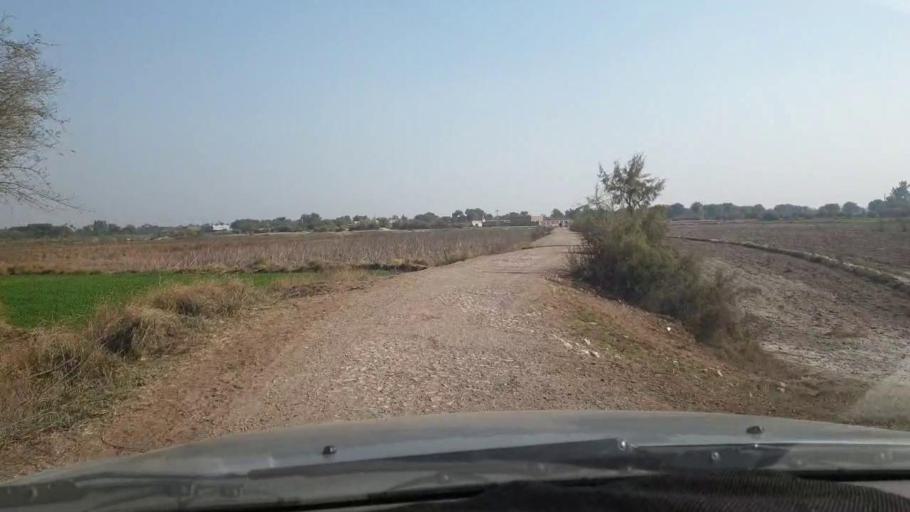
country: PK
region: Sindh
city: Mirpur Mathelo
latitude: 27.9316
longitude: 69.5645
